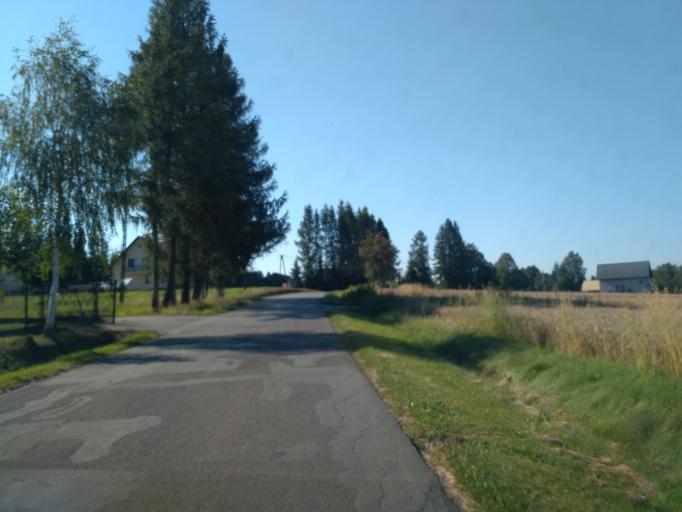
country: PL
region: Subcarpathian Voivodeship
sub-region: Powiat strzyzowski
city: Wysoka Strzyzowska
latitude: 49.8428
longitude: 21.7345
